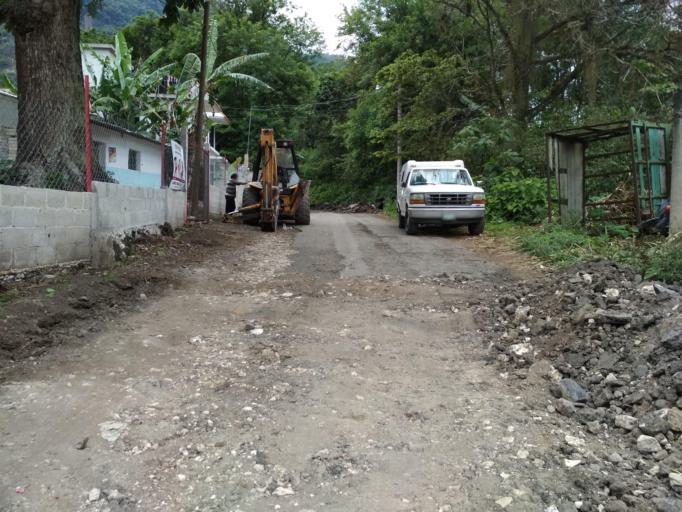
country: MX
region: Veracruz
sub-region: Jilotepec
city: El Pueblito (Garbanzal)
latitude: 19.6180
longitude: -96.9260
